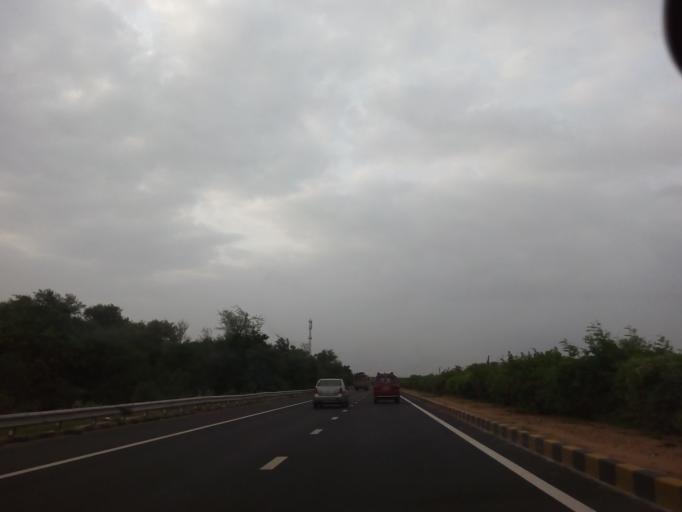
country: IN
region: Gujarat
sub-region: Kheda
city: Mahemdavad
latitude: 22.8974
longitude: 72.7790
